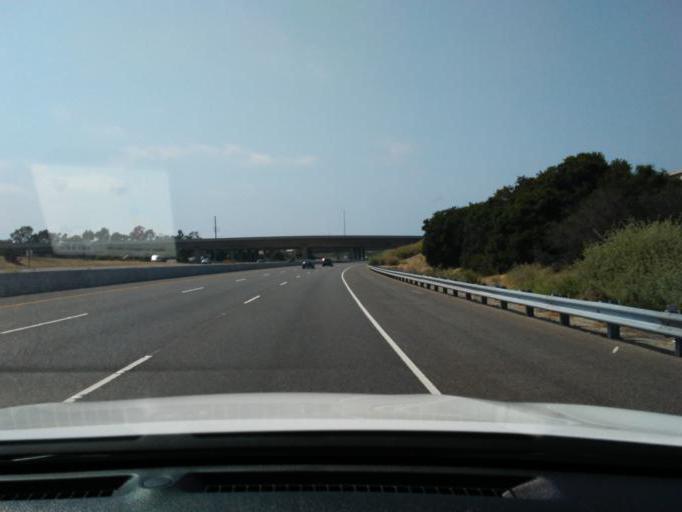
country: US
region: California
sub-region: Orange County
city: San Joaquin Hills
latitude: 33.6394
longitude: -117.8577
